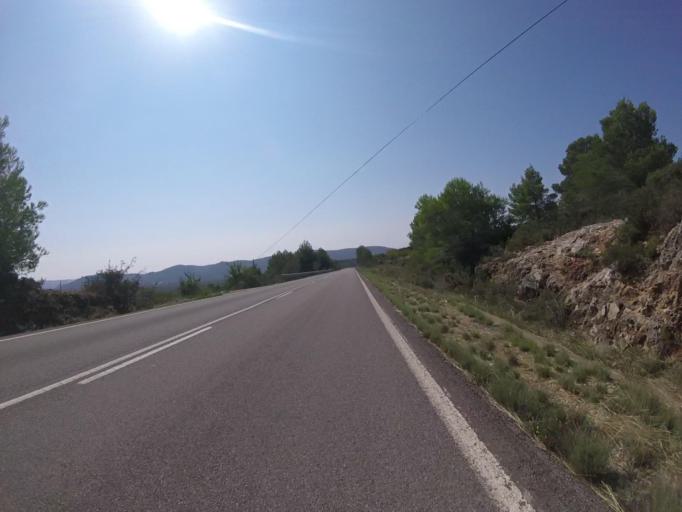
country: ES
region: Valencia
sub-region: Provincia de Castello
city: Adzaneta
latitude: 40.2413
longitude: -0.1891
